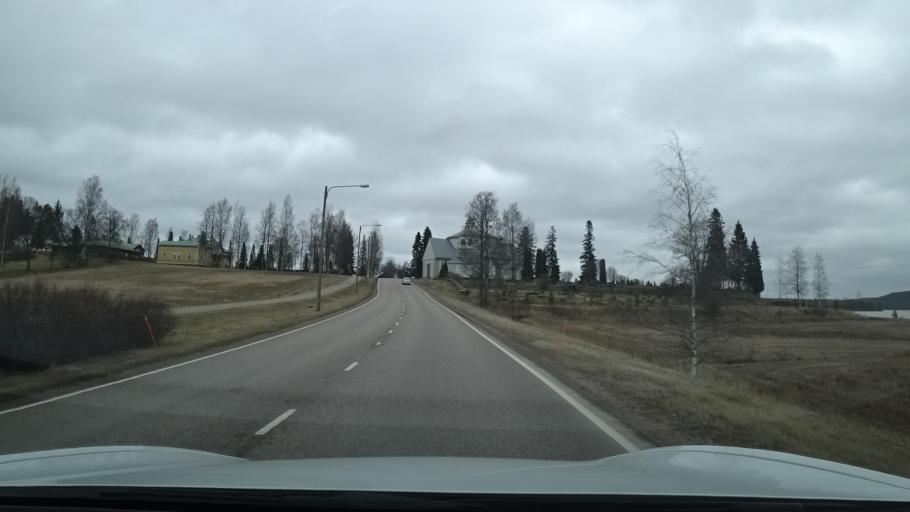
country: FI
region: Uusimaa
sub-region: Porvoo
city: Myrskylae
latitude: 60.6656
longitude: 25.8488
